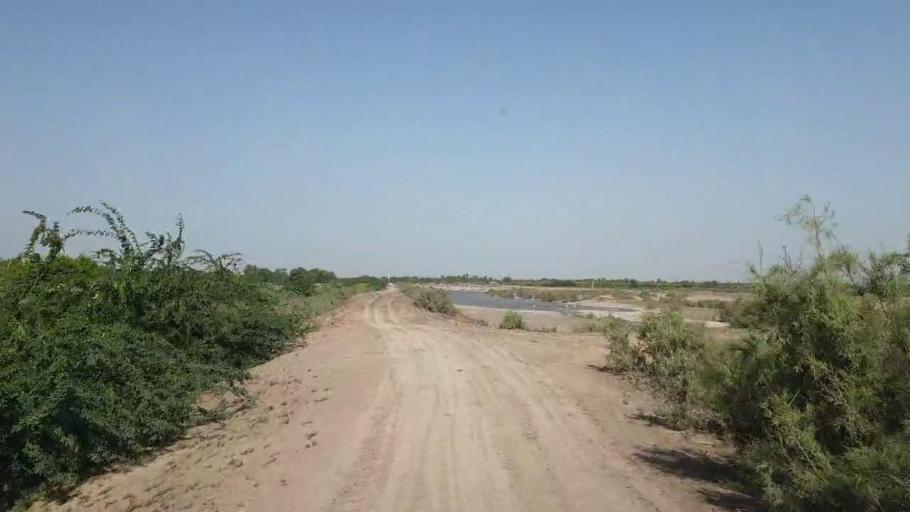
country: PK
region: Sindh
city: Tando Bago
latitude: 24.6597
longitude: 69.0691
